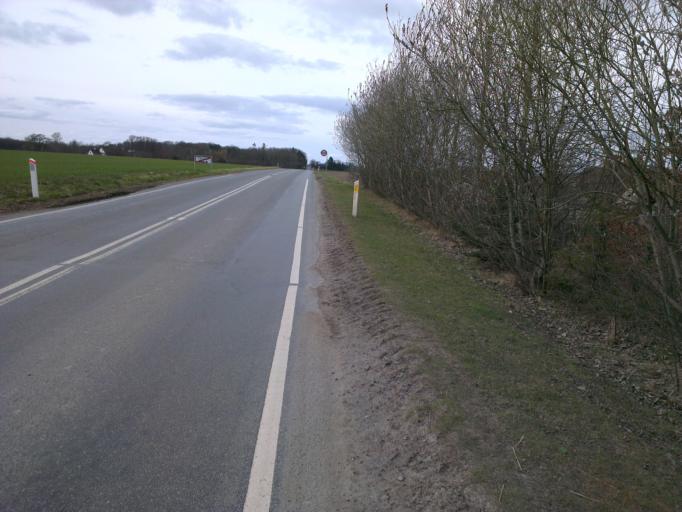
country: DK
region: Capital Region
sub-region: Frederikssund Kommune
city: Frederikssund
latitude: 55.8116
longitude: 12.0221
